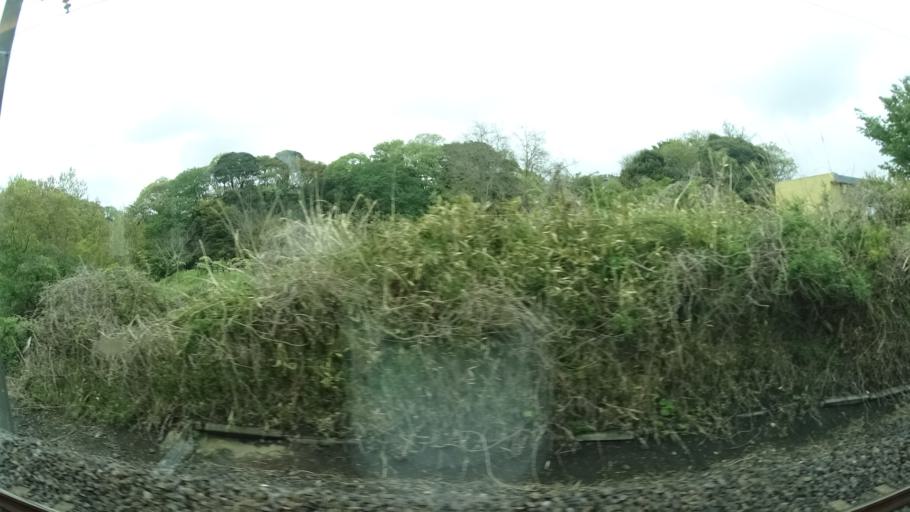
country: JP
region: Ibaraki
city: Funaishikawa
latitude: 36.5000
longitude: 140.6105
